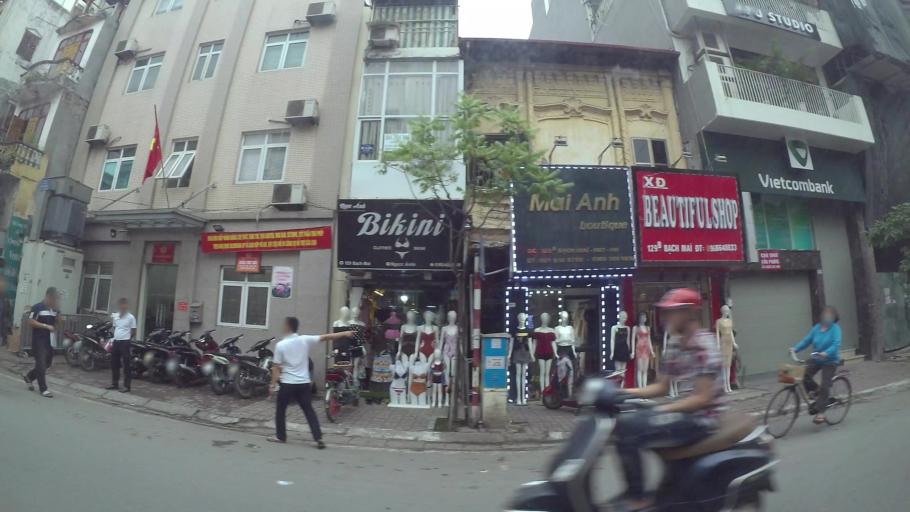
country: VN
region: Ha Noi
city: Hai BaTrung
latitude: 21.0062
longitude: 105.8512
